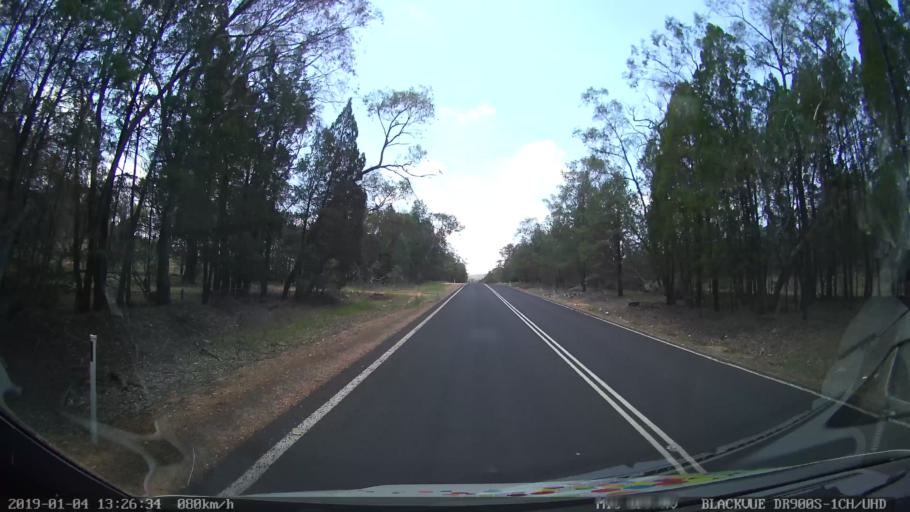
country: AU
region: New South Wales
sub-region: Parkes
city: Peak Hill
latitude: -32.6796
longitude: 148.5586
